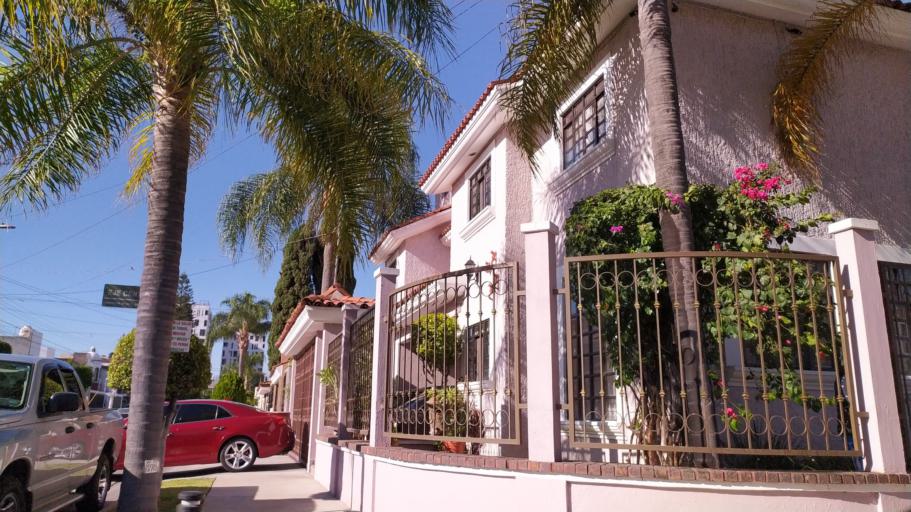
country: MX
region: Jalisco
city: Guadalajara
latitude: 20.6587
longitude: -103.4249
